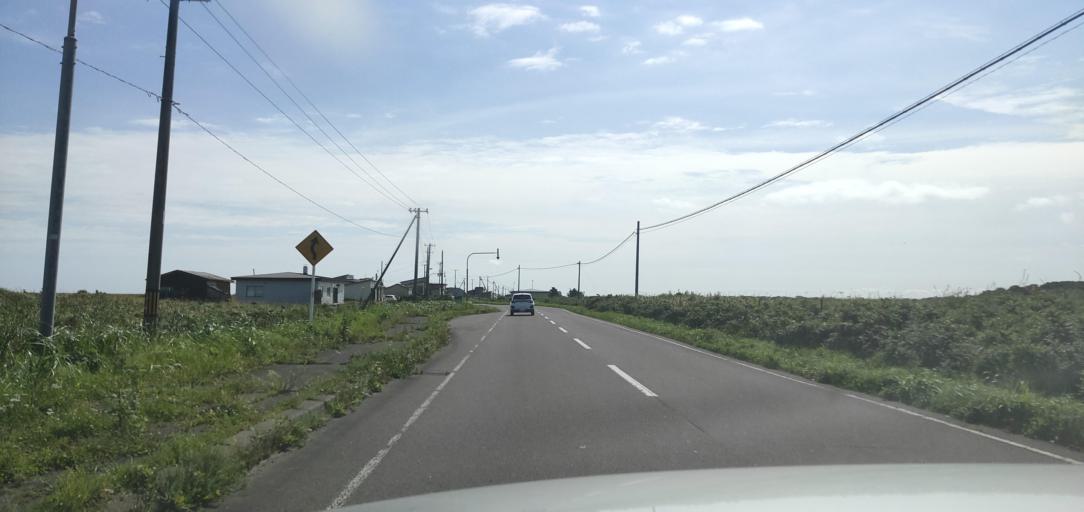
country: JP
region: Hokkaido
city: Shibetsu
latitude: 43.6328
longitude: 145.1825
